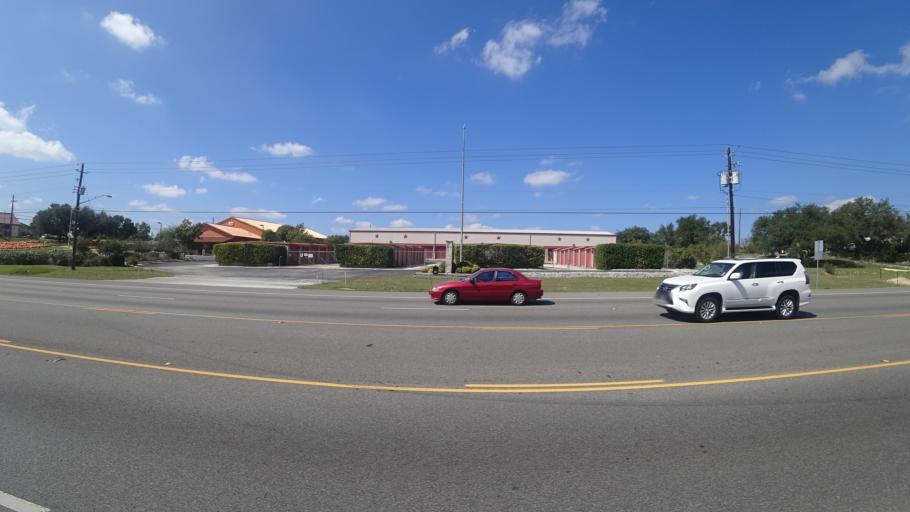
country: US
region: Texas
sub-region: Travis County
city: Lakeway
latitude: 30.3778
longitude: -97.9462
